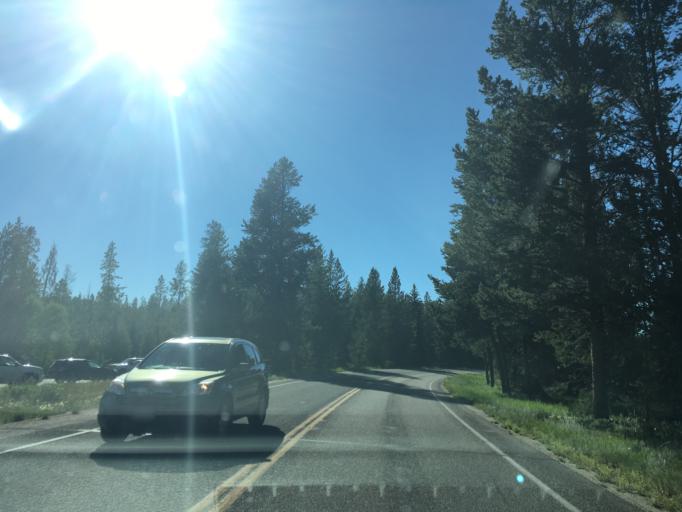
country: US
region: Wyoming
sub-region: Teton County
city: Jackson
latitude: 43.8455
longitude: -110.5153
